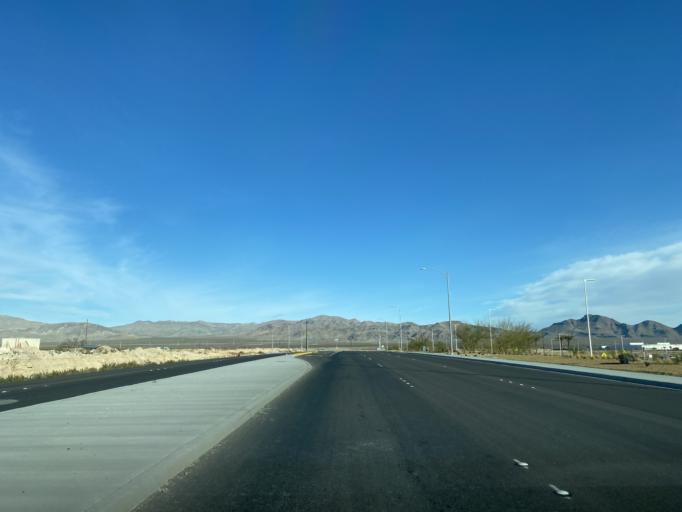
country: US
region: Nevada
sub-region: Clark County
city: Nellis Air Force Base
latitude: 36.2670
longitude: -115.0432
